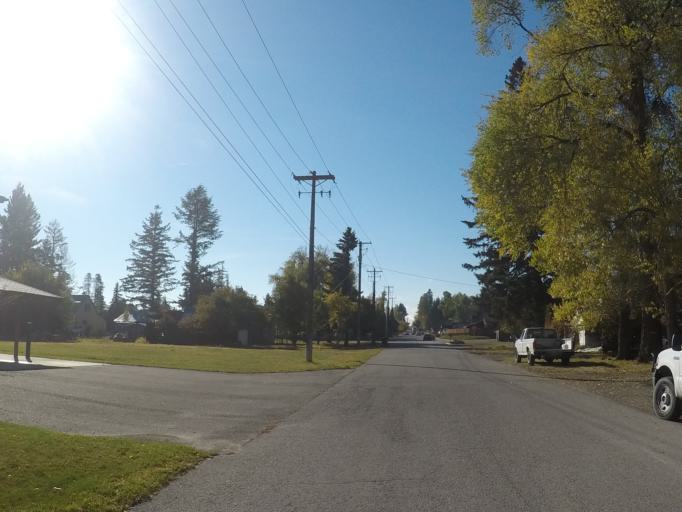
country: US
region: Montana
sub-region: Flathead County
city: Whitefish
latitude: 48.4118
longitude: -114.3521
